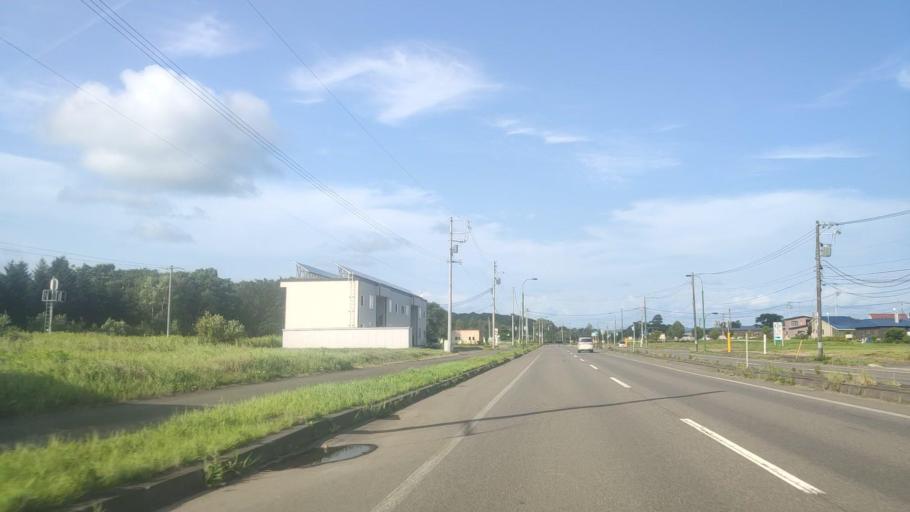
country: JP
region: Hokkaido
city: Chitose
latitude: 42.7670
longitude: 141.8168
